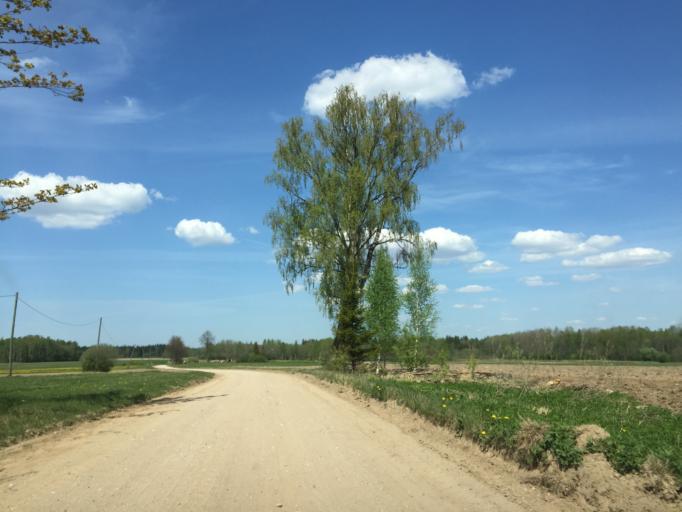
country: LV
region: Limbazu Rajons
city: Limbazi
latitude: 57.3541
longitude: 24.6471
